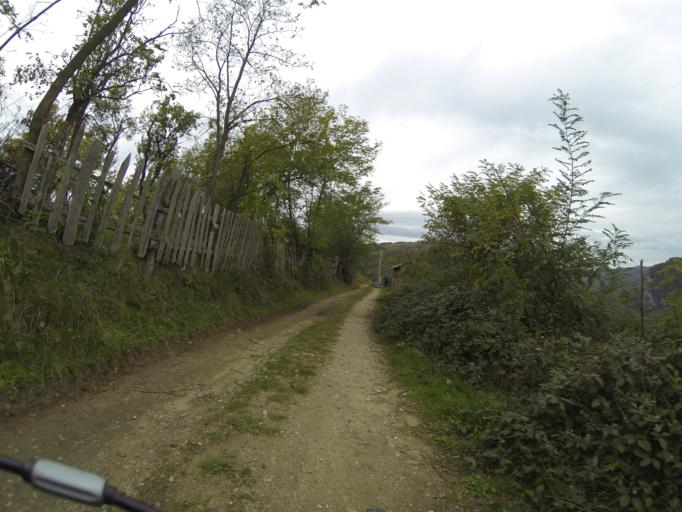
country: RO
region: Gorj
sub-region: Comuna Tismana
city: Sohodol
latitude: 45.0572
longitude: 22.8935
